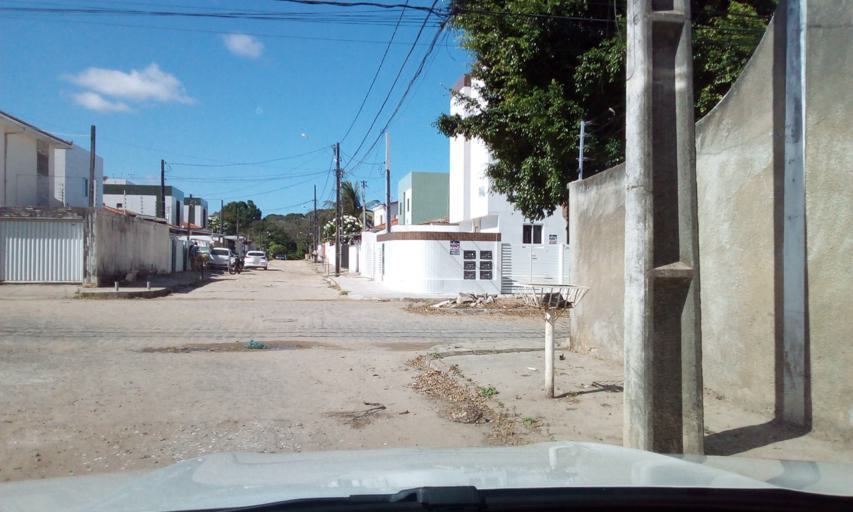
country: BR
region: Paraiba
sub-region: Joao Pessoa
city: Joao Pessoa
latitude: -7.1814
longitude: -34.8587
